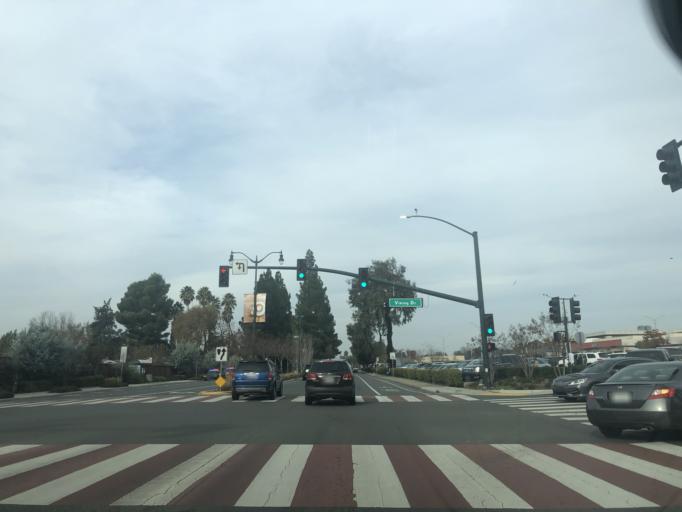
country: US
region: California
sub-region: Contra Costa County
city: Pleasant Hill
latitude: 37.9669
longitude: -122.0626
